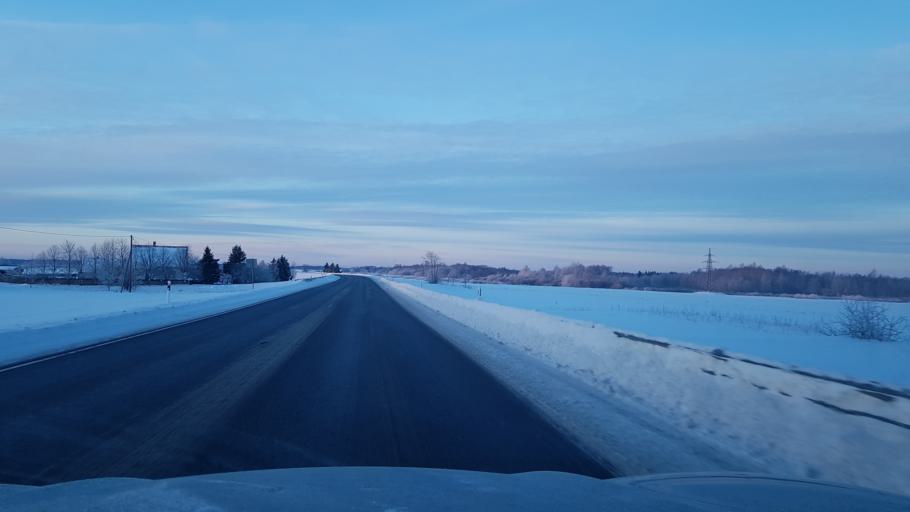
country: EE
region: Ida-Virumaa
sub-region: Narva-Joesuu linn
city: Narva-Joesuu
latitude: 59.4051
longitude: 28.0208
